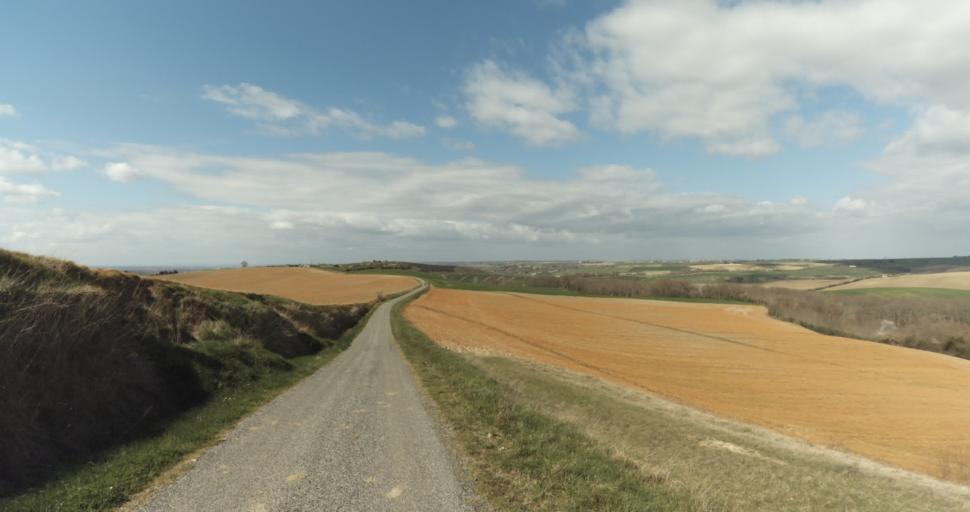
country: FR
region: Midi-Pyrenees
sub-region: Departement de la Haute-Garonne
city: Auterive
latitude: 43.3584
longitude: 1.5158
